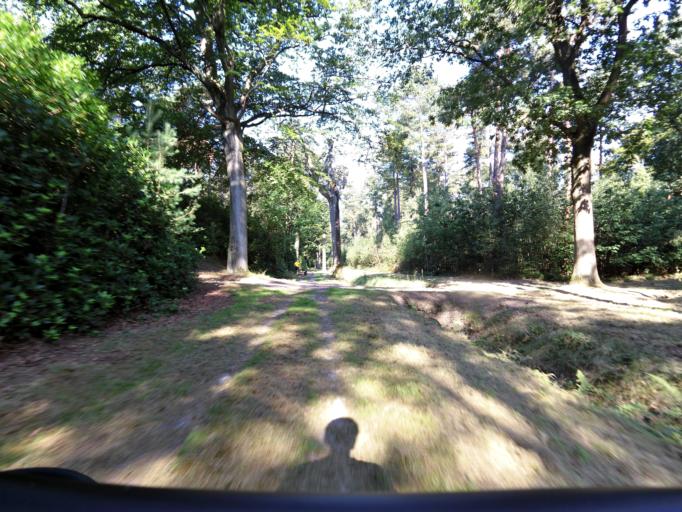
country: BE
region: Flanders
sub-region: Provincie Antwerpen
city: Stabroek
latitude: 51.3583
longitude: 4.3753
